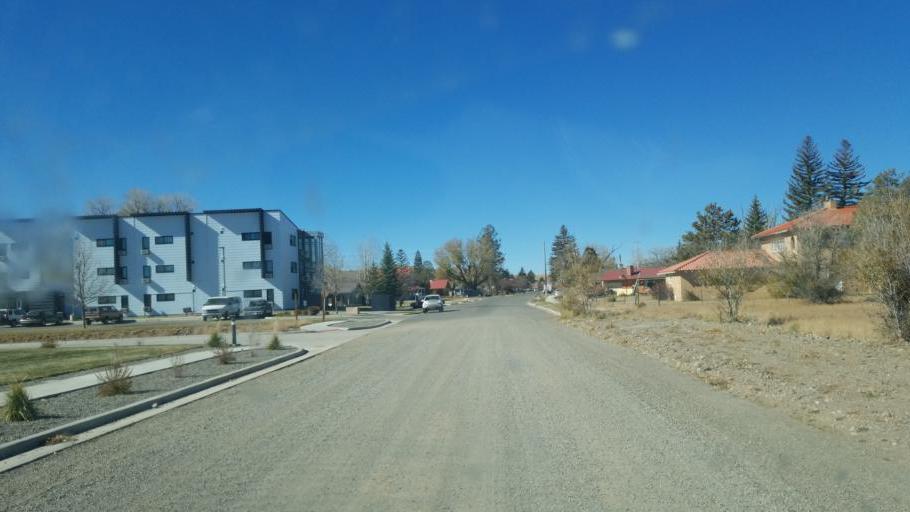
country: US
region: Colorado
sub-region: Rio Grande County
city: Del Norte
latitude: 37.6771
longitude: -106.3449
